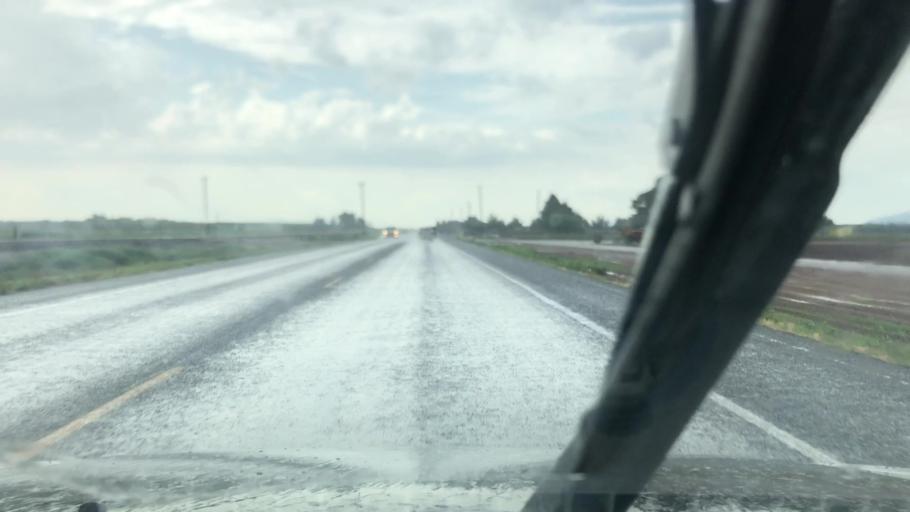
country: US
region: New Mexico
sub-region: Dona Ana County
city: Mesquite
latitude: 32.1725
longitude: -106.7016
